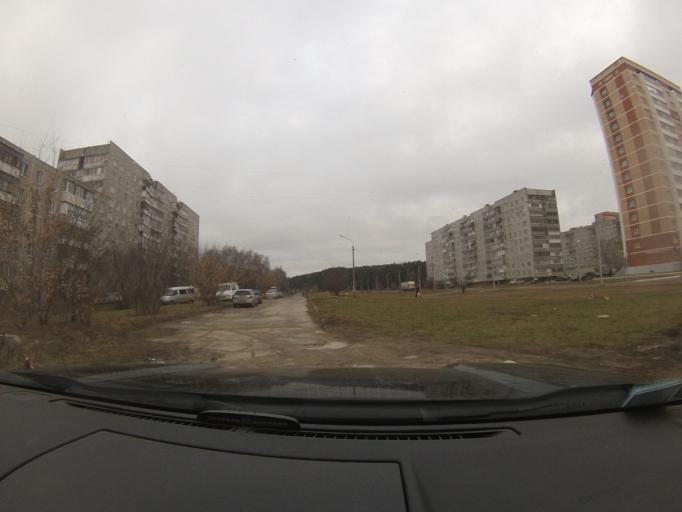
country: RU
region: Moskovskaya
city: Peski
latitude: 55.2740
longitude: 38.7532
